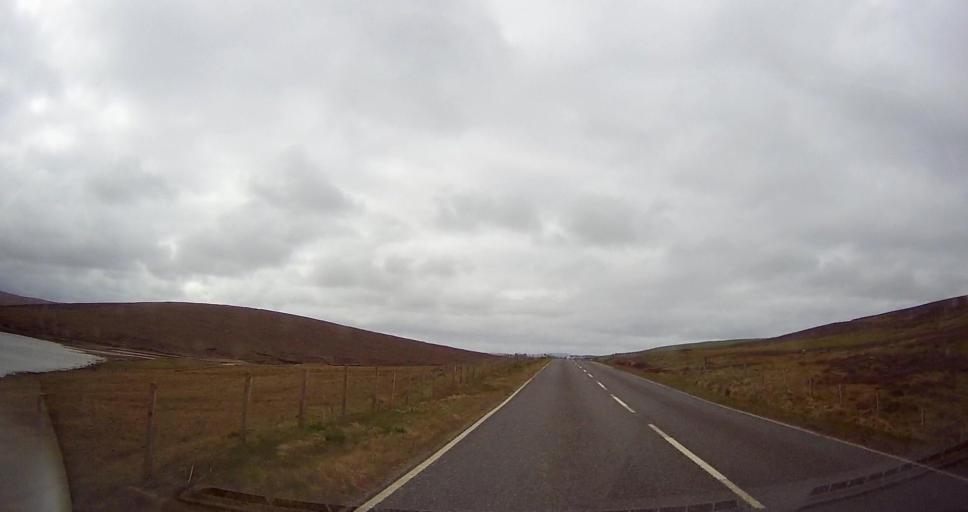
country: GB
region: Scotland
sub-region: Shetland Islands
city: Lerwick
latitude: 60.2501
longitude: -1.3766
